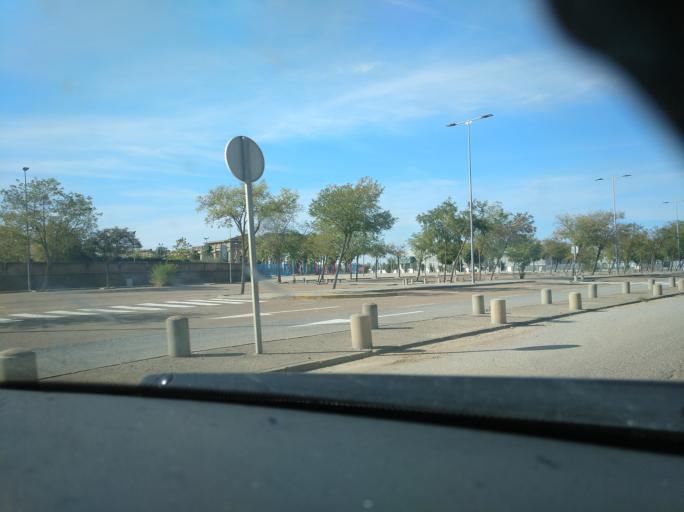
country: ES
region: Extremadura
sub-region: Provincia de Badajoz
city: Badajoz
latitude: 38.8790
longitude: -7.0256
